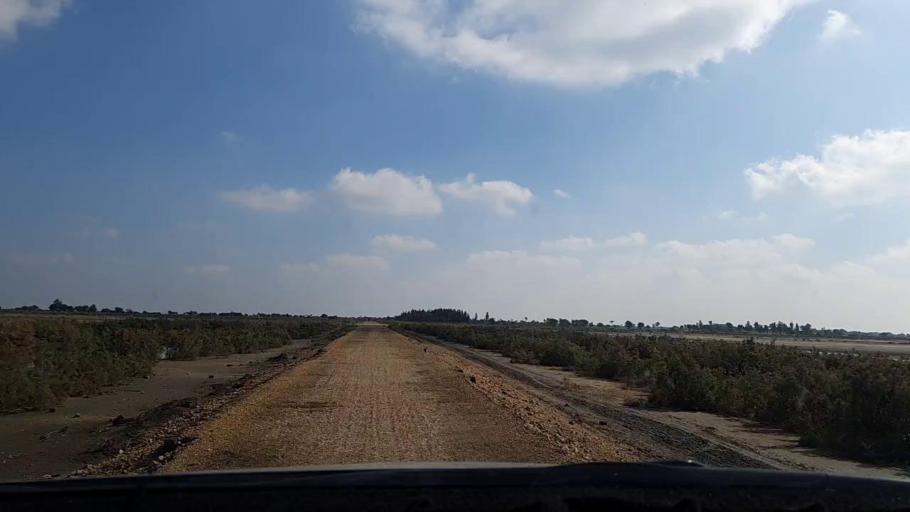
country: PK
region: Sindh
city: Pithoro
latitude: 25.7332
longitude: 69.2824
